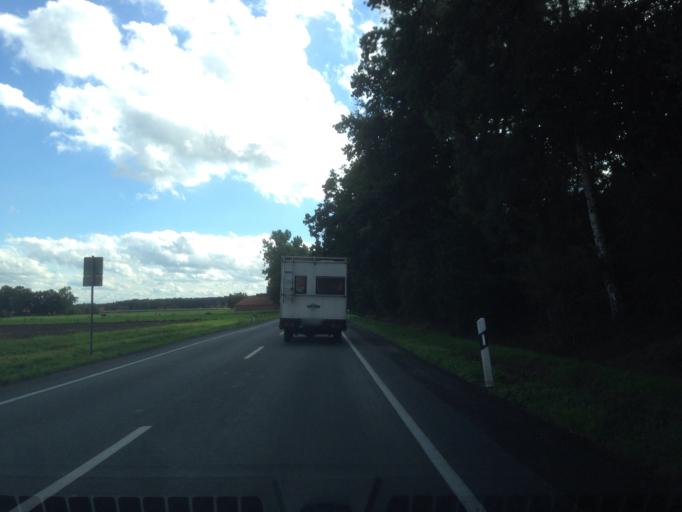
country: DE
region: North Rhine-Westphalia
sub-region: Regierungsbezirk Munster
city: Senden
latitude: 51.8617
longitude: 7.5483
